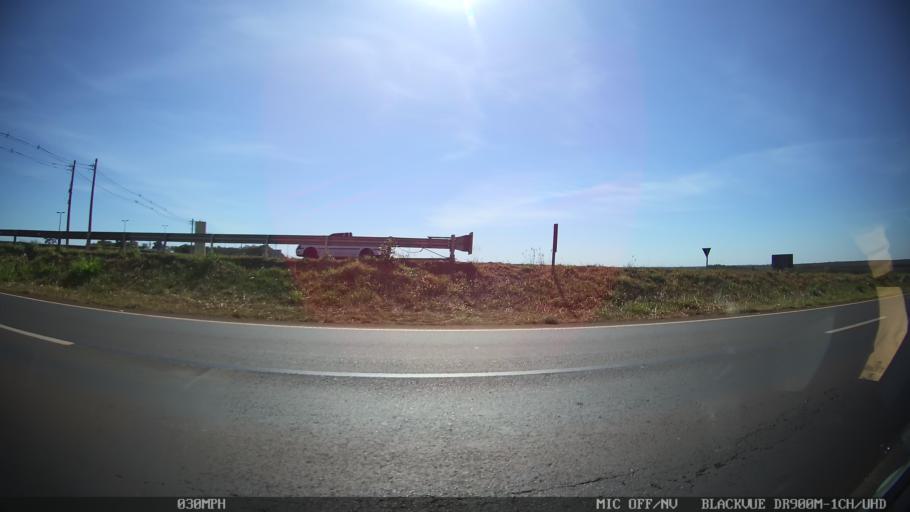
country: BR
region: Sao Paulo
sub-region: Barretos
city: Barretos
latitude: -20.5273
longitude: -48.5888
